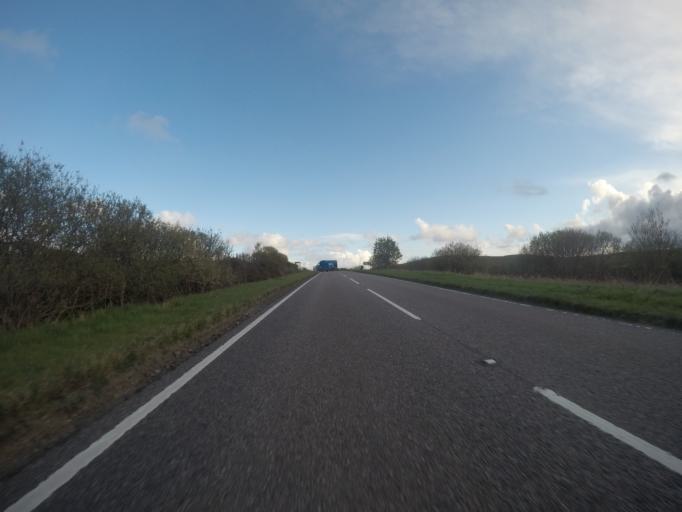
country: GB
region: Scotland
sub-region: Highland
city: Portree
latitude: 57.4770
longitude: -6.2999
